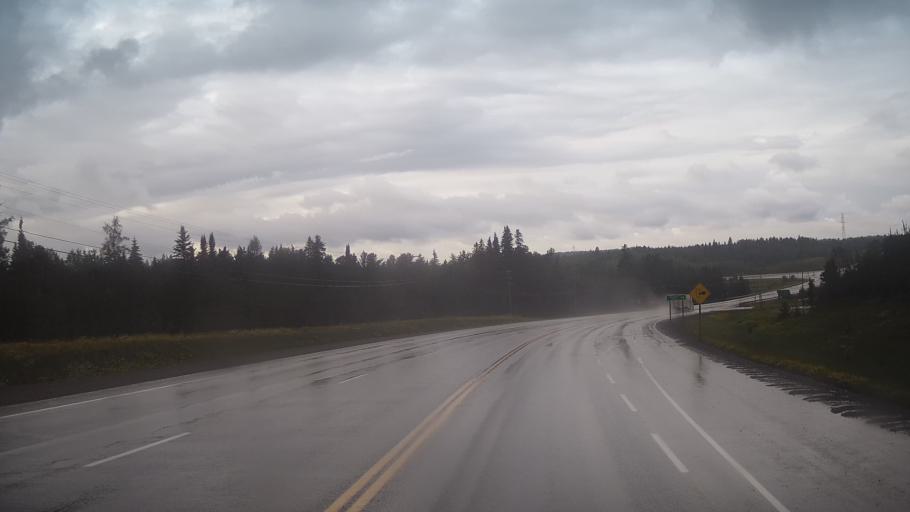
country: CA
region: Ontario
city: Neebing
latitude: 48.5962
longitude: -89.8955
